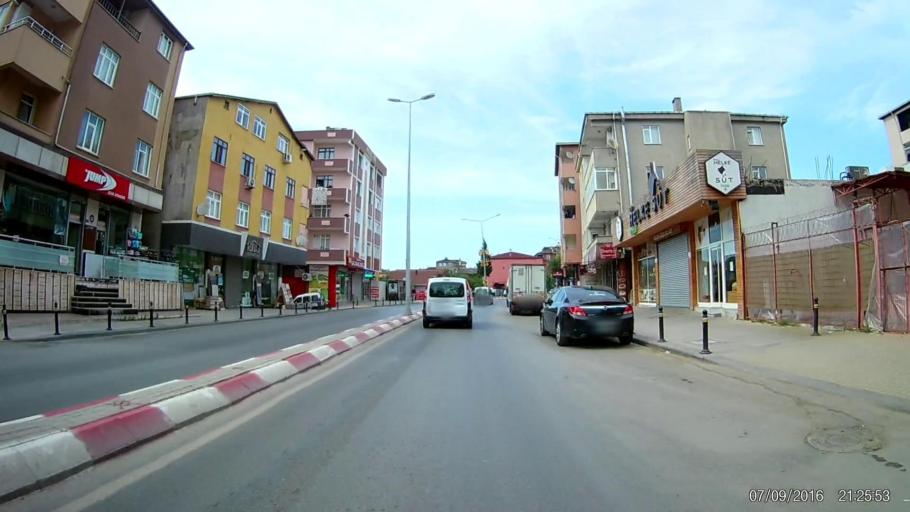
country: TR
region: Istanbul
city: Sultanbeyli
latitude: 40.9801
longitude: 29.2658
